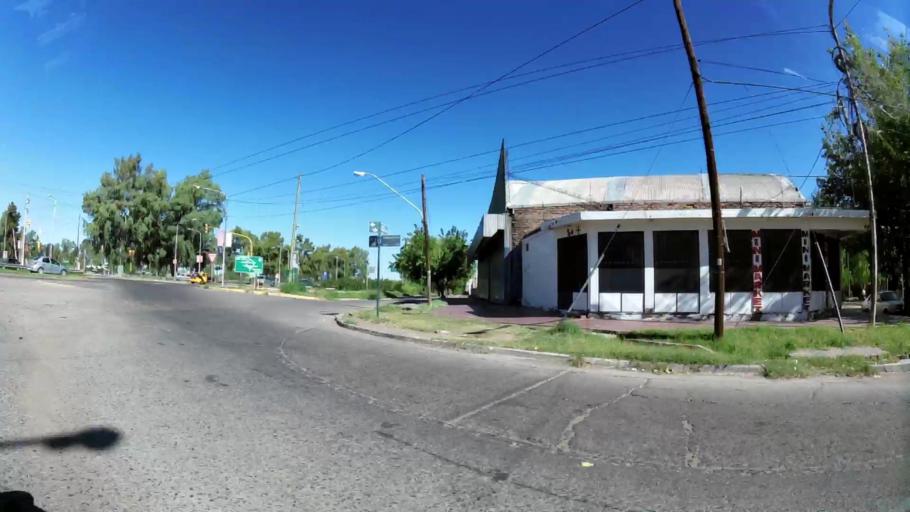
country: AR
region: Mendoza
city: Las Heras
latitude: -32.8424
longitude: -68.8034
